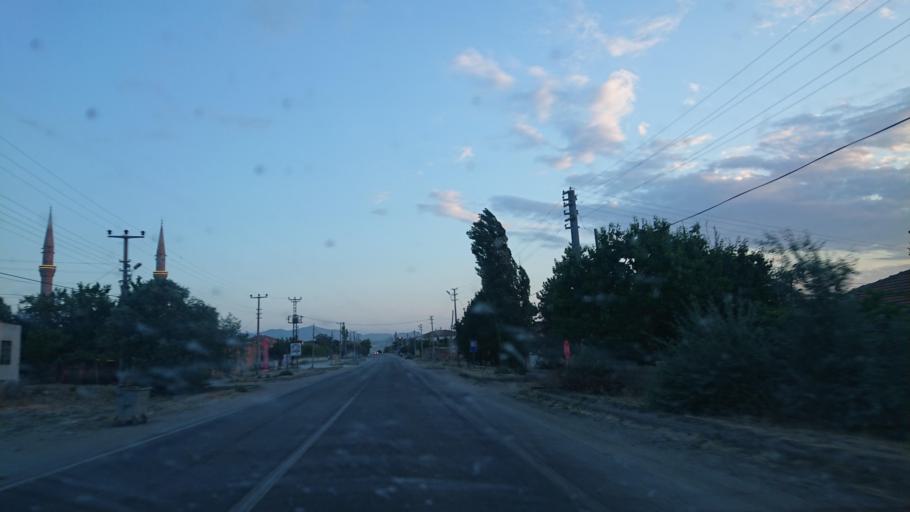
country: TR
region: Aksaray
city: Balci
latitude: 38.7916
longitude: 34.1236
